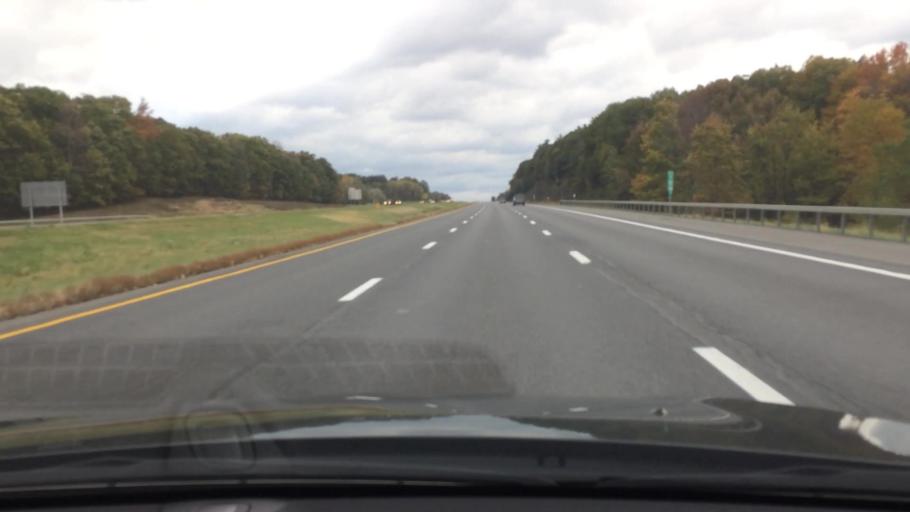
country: US
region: New York
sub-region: Rensselaer County
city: East Greenbush
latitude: 42.6149
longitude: -73.6891
